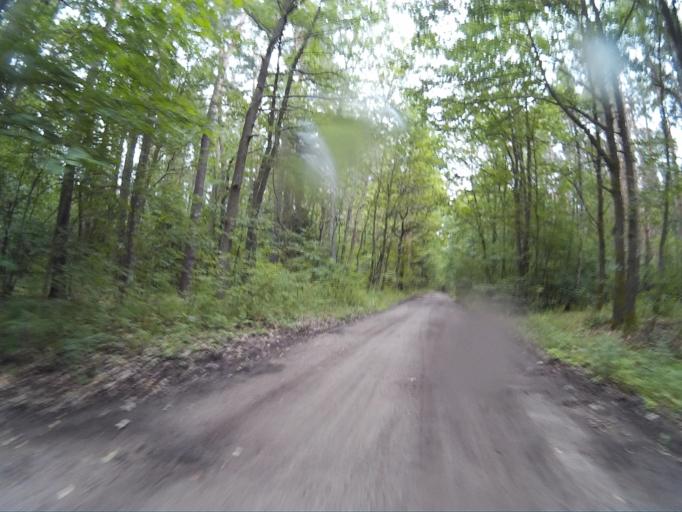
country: PL
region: Kujawsko-Pomorskie
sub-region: Powiat tucholski
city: Tuchola
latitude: 53.5501
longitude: 17.8792
